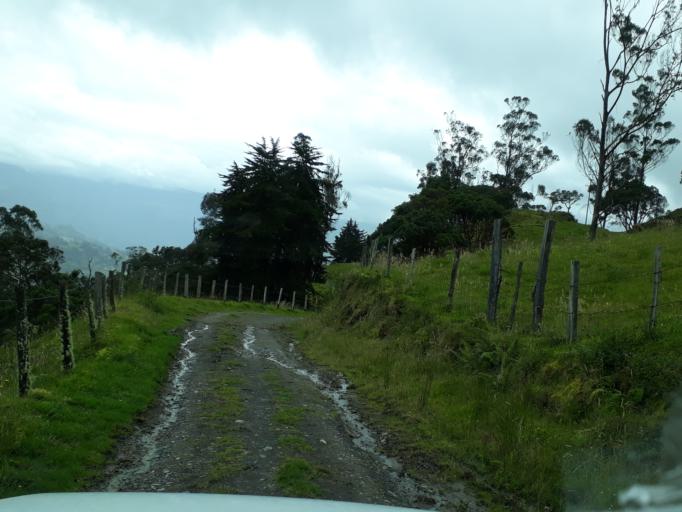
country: CO
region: Cundinamarca
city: Junin
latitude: 4.7354
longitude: -73.6257
